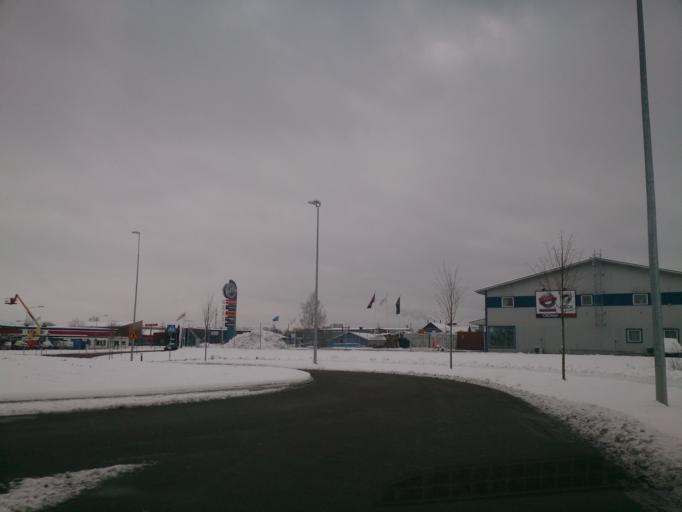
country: SE
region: OEstergoetland
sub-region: Linkopings Kommun
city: Linkoping
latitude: 58.4316
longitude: 15.6104
